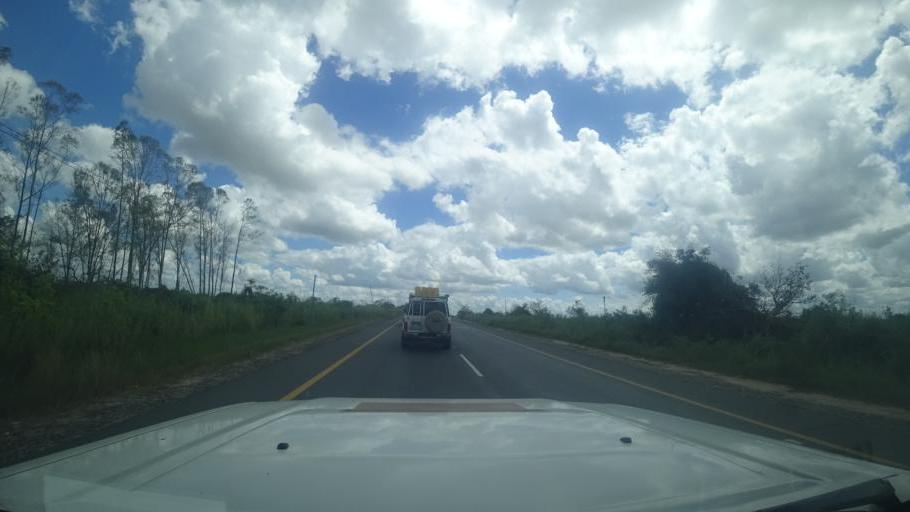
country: MZ
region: Sofala
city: Dondo
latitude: -19.5721
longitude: 34.7004
